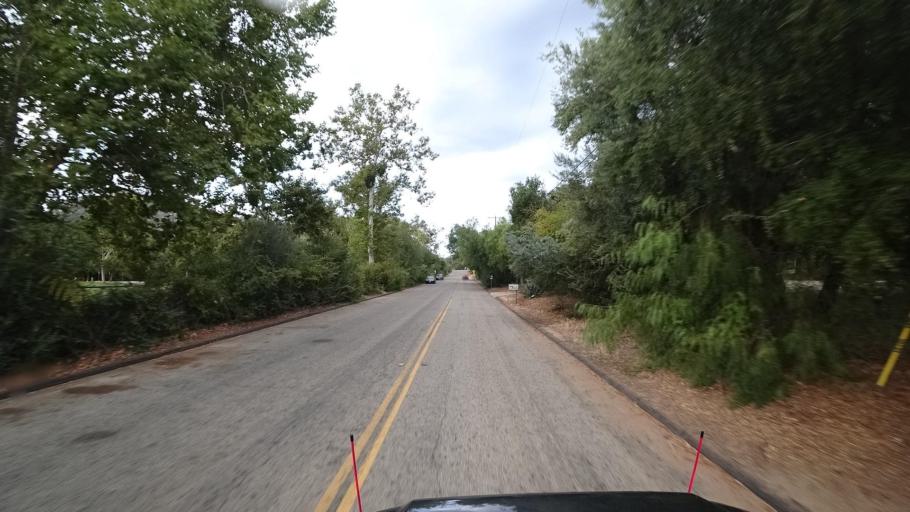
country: US
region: California
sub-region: San Diego County
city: Ramona
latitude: 32.9997
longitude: -116.9370
